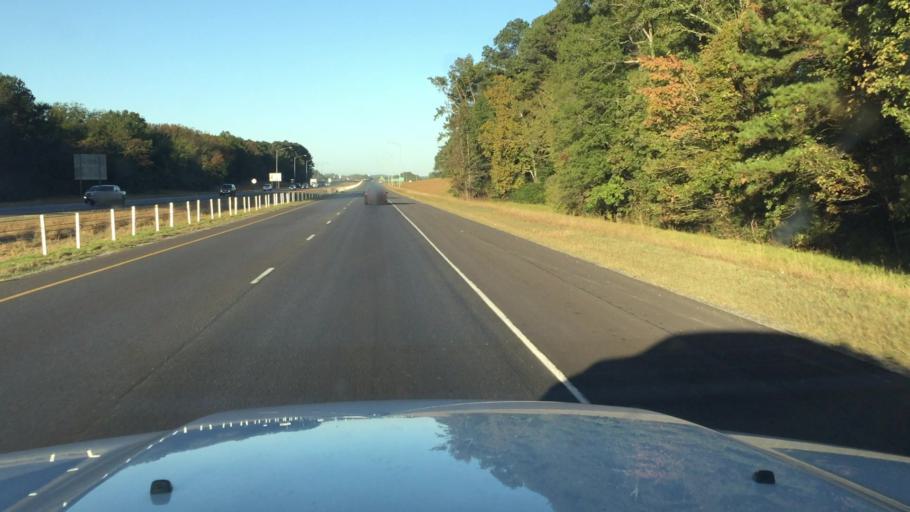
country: US
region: Alabama
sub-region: Etowah County
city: Gadsden
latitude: 33.9919
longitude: -86.0264
